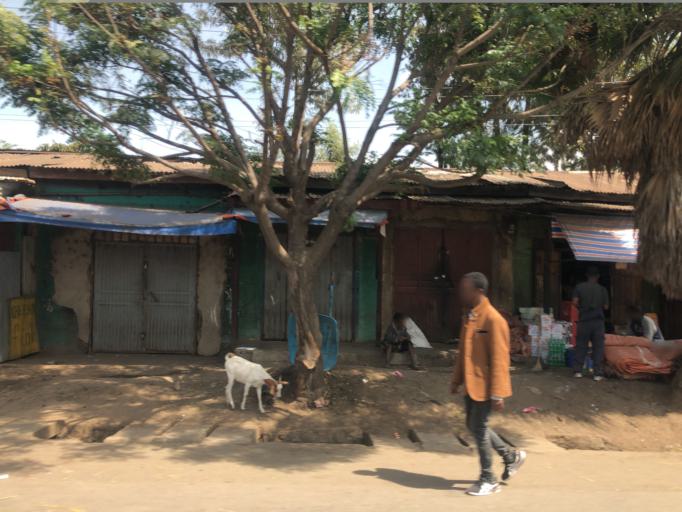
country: ET
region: Oromiya
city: Shashemene
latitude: 7.2670
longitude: 38.6568
